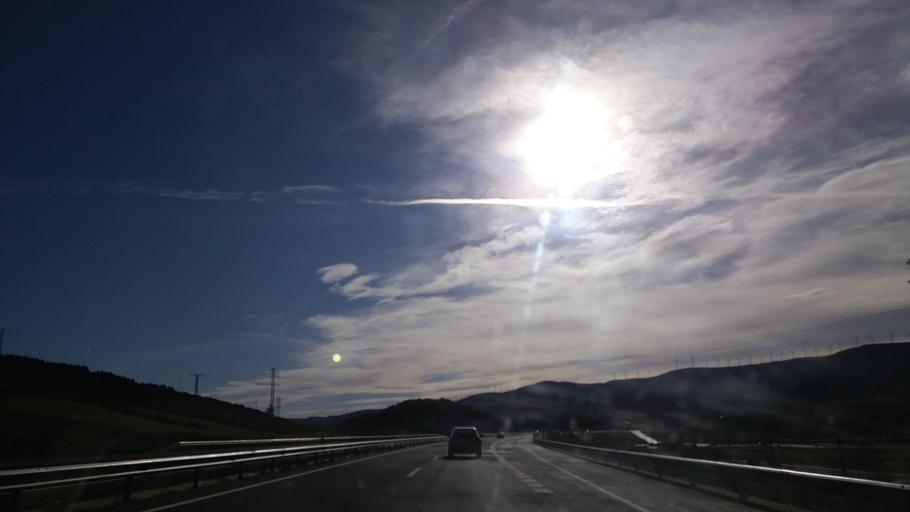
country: ES
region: Navarre
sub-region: Provincia de Navarra
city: Monreal
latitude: 42.6964
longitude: -1.4824
